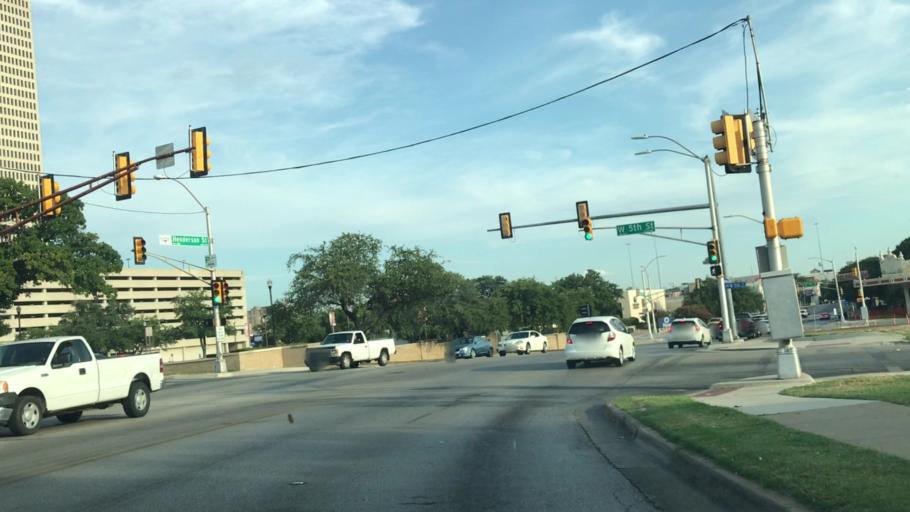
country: US
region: Texas
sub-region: Tarrant County
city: Fort Worth
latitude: 32.7521
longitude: -97.3376
